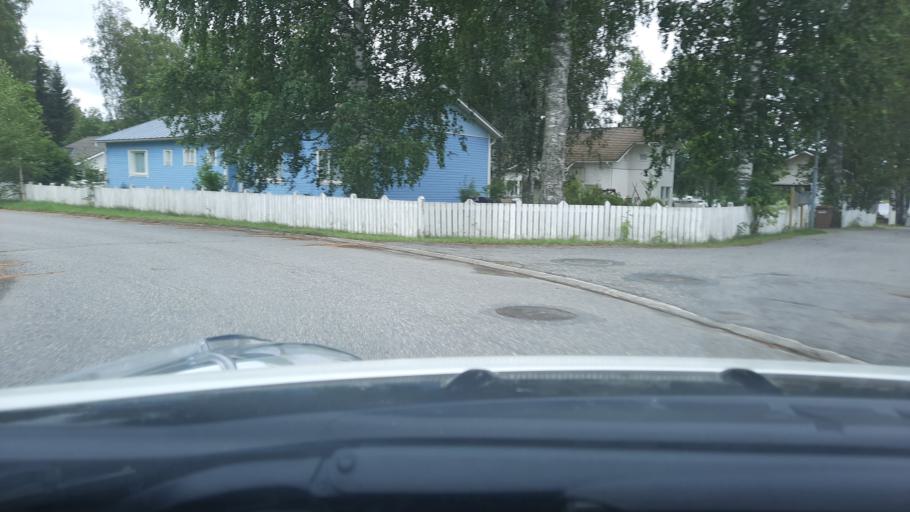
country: FI
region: North Karelia
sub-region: Joensuu
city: Joensuu
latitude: 62.6106
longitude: 29.8317
